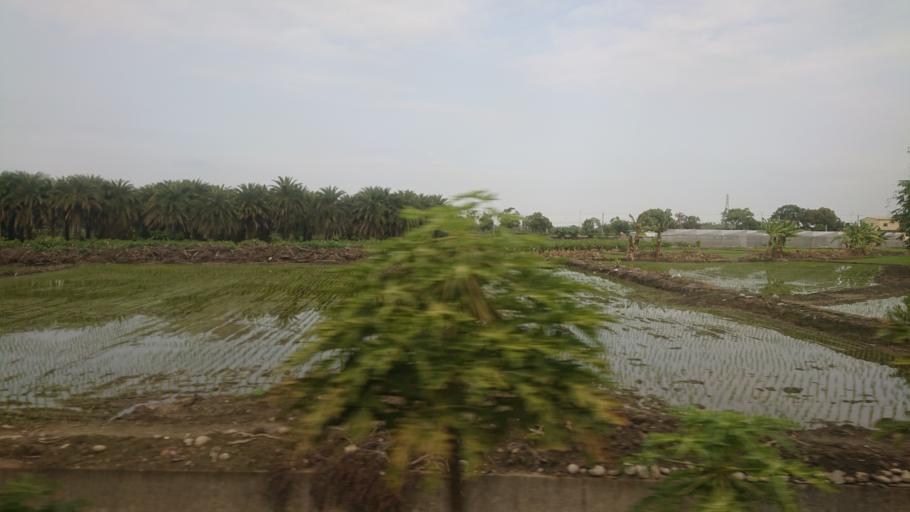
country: TW
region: Taiwan
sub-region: Yunlin
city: Douliu
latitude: 23.7628
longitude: 120.6185
